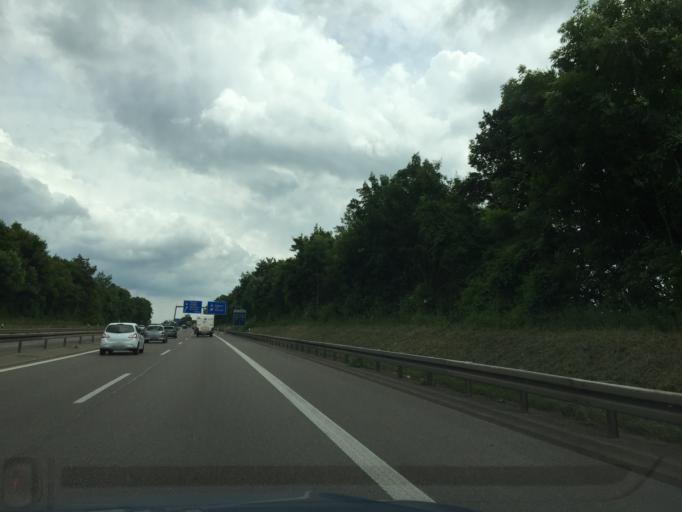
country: DE
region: Baden-Wuerttemberg
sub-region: Tuebingen Region
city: Ulm
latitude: 48.3654
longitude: 9.9844
